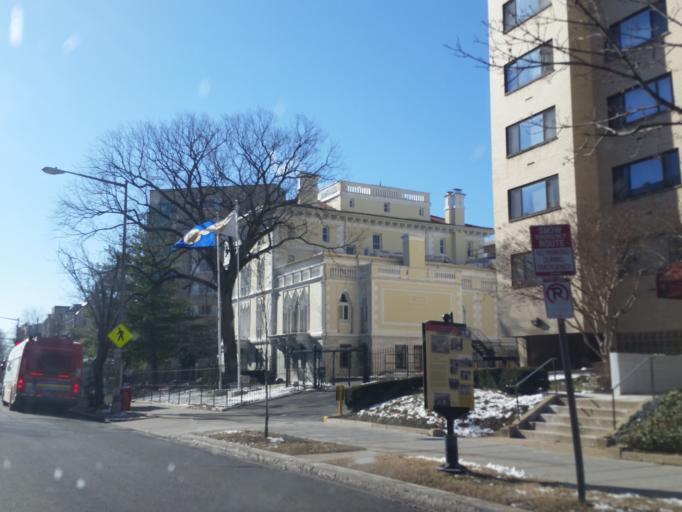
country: US
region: Washington, D.C.
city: Washington, D.C.
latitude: 38.9240
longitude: -77.0366
